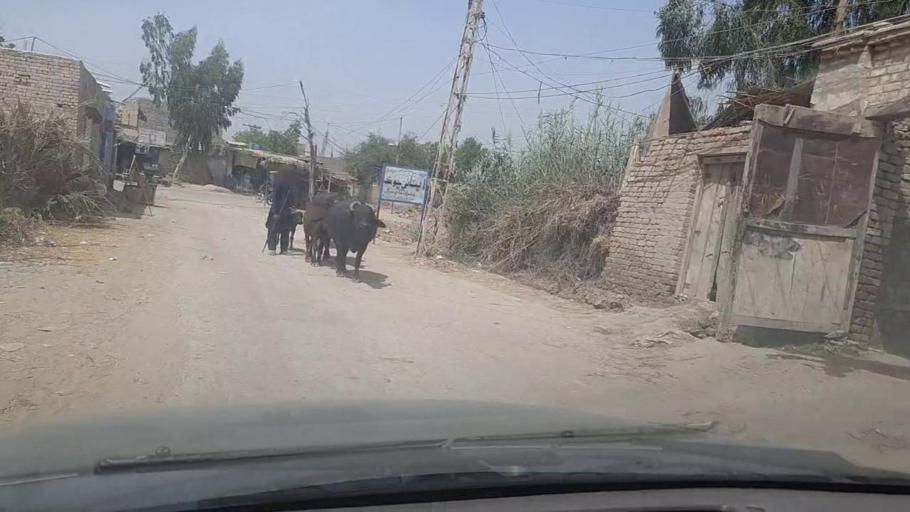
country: PK
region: Sindh
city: Madeji
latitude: 27.7986
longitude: 68.4084
